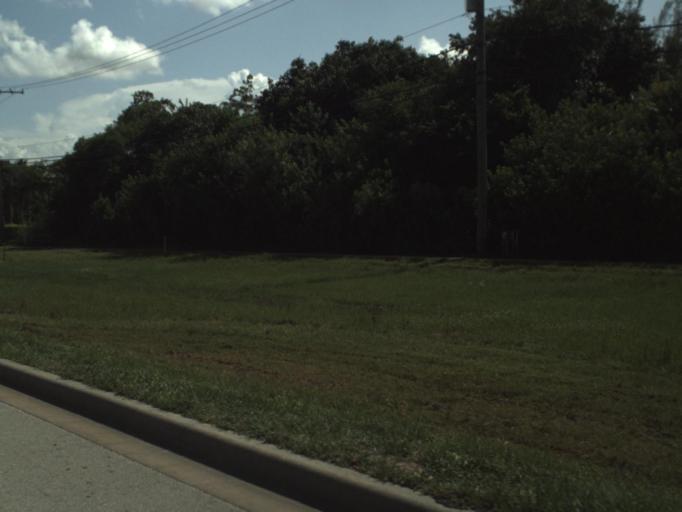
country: US
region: Florida
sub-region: Palm Beach County
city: Wellington
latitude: 26.6606
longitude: -80.2032
